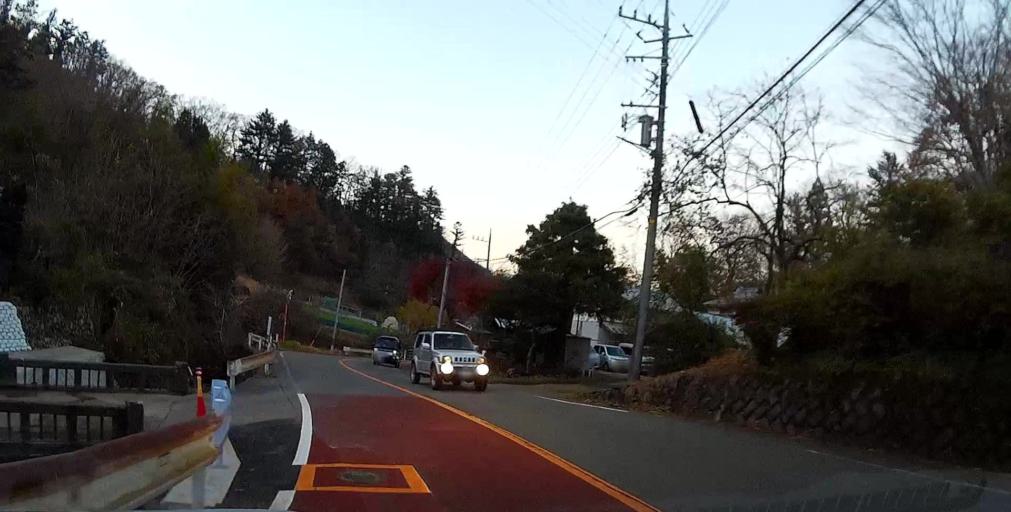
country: JP
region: Yamanashi
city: Uenohara
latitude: 35.5863
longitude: 139.1731
